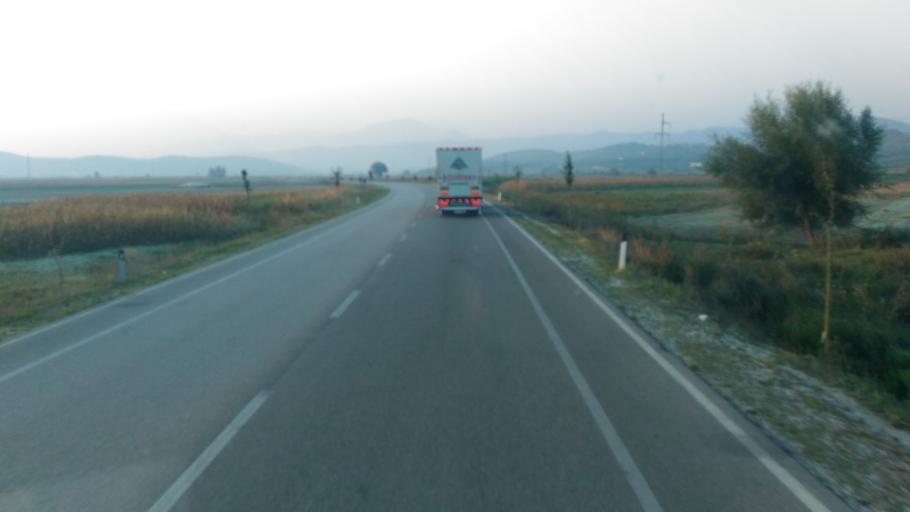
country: AL
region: Fier
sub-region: Rrethi i Fierit
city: Cakran
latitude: 40.5757
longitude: 19.6222
